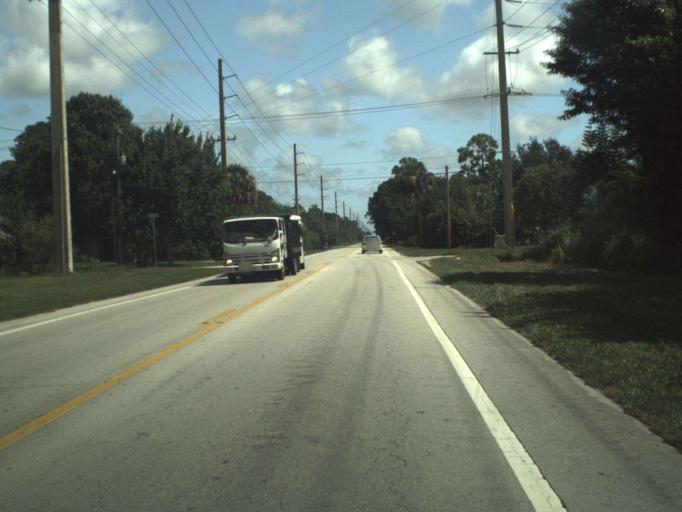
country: US
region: Florida
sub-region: Indian River County
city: West Vero Corridor
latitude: 27.6528
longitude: -80.4465
